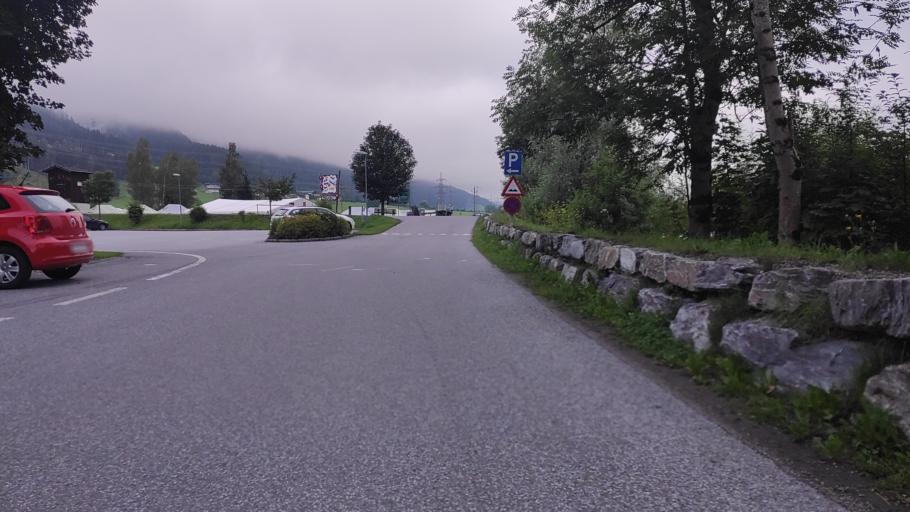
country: AT
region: Salzburg
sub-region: Politischer Bezirk Zell am See
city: Niedernsill
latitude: 47.2806
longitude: 12.6457
